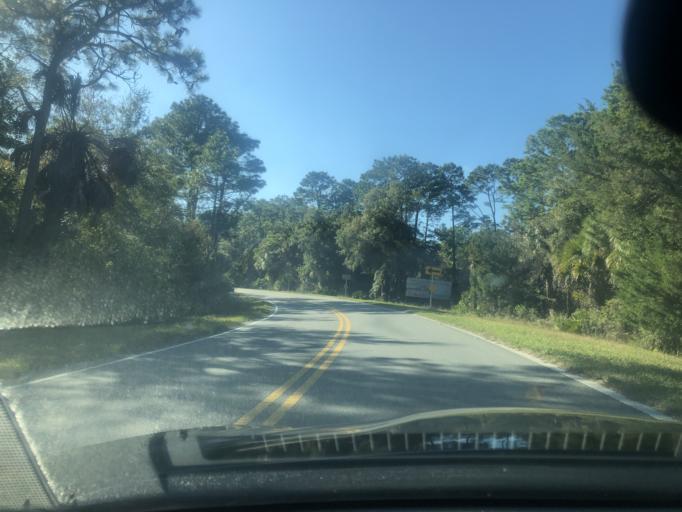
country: US
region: Florida
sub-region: Citrus County
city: Homosassa Springs
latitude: 28.8184
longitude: -82.5591
